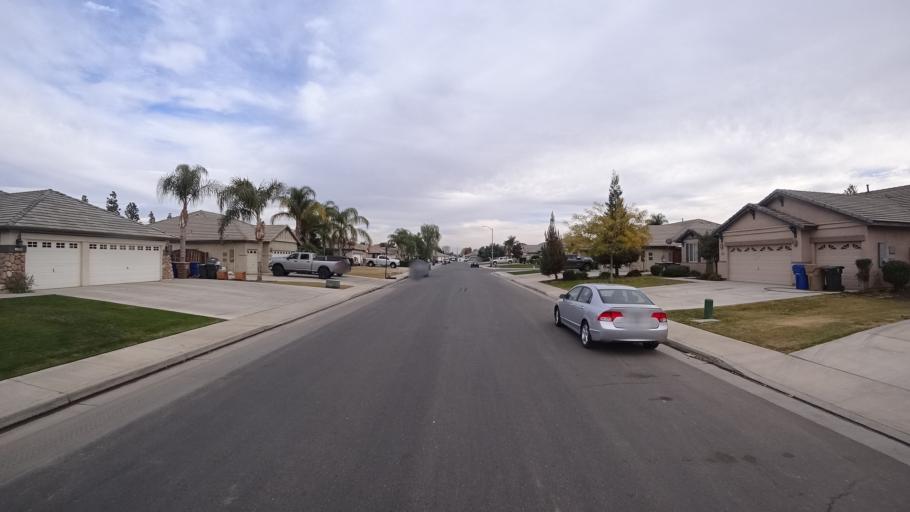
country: US
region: California
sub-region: Kern County
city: Rosedale
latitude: 35.4261
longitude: -119.1345
